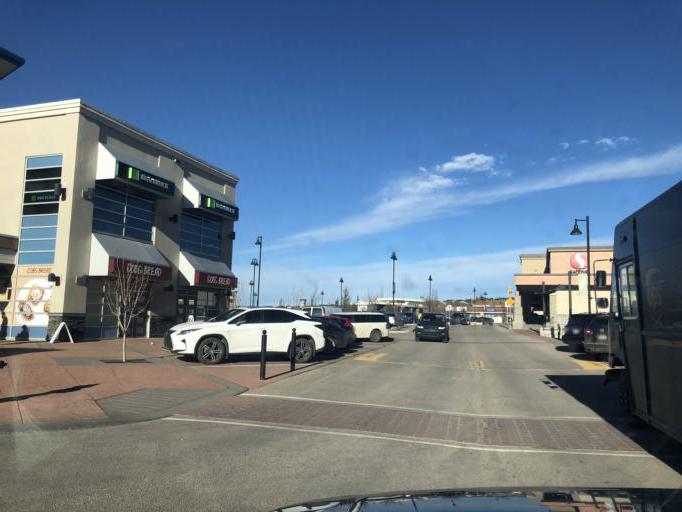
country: CA
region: Alberta
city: Calgary
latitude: 51.0401
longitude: -114.2085
